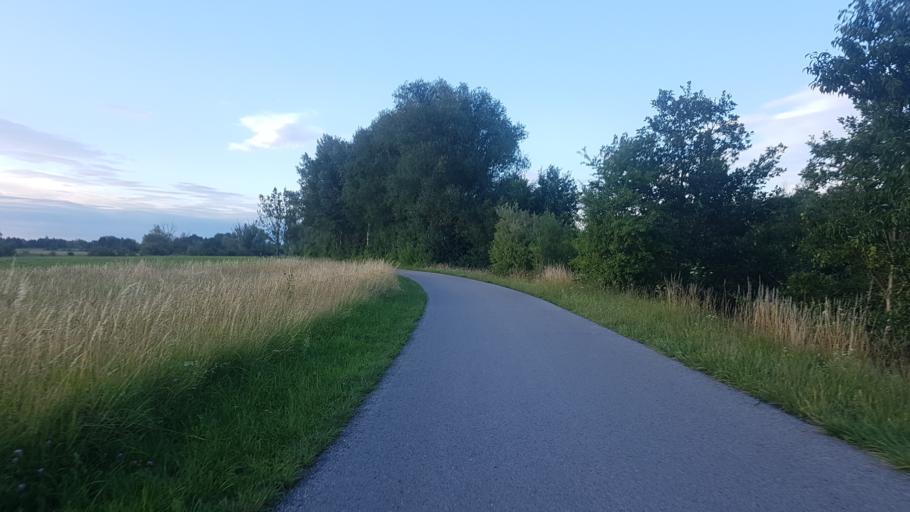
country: DE
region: Bavaria
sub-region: Regierungsbezirk Mittelfranken
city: Muhr am See
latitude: 49.1439
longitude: 10.7012
